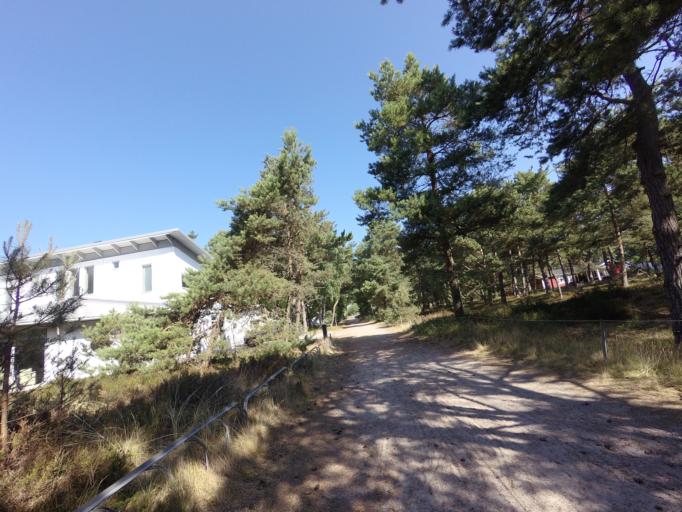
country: SE
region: Skane
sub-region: Vellinge Kommun
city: Ljunghusen
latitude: 55.3947
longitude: 12.9373
